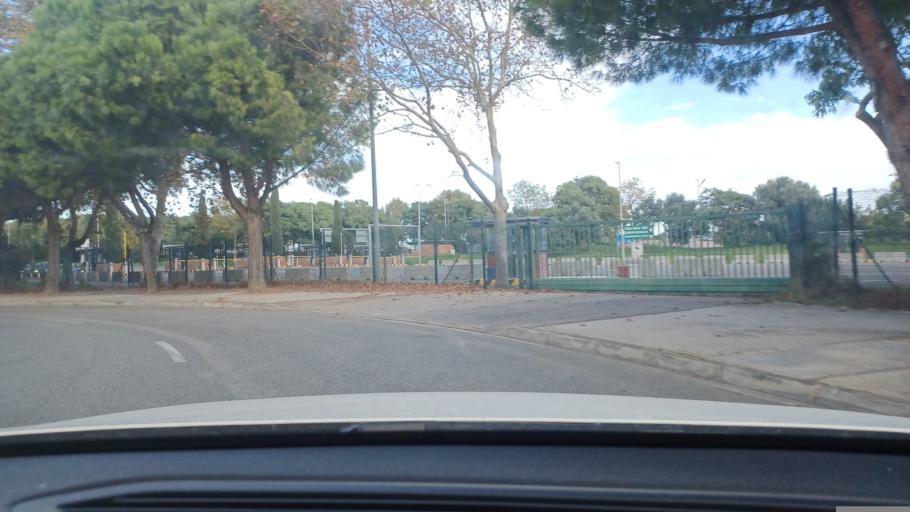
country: ES
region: Catalonia
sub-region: Provincia de Tarragona
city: Salou
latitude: 41.0949
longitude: 1.1521
